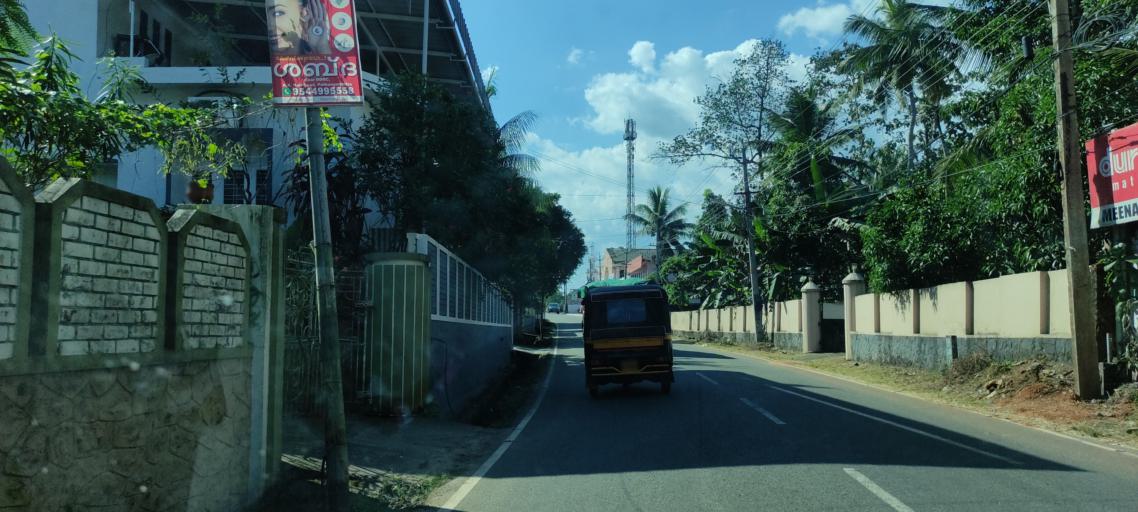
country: IN
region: Kerala
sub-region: Pattanamtitta
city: Pathanamthitta
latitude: 9.2310
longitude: 76.7525
